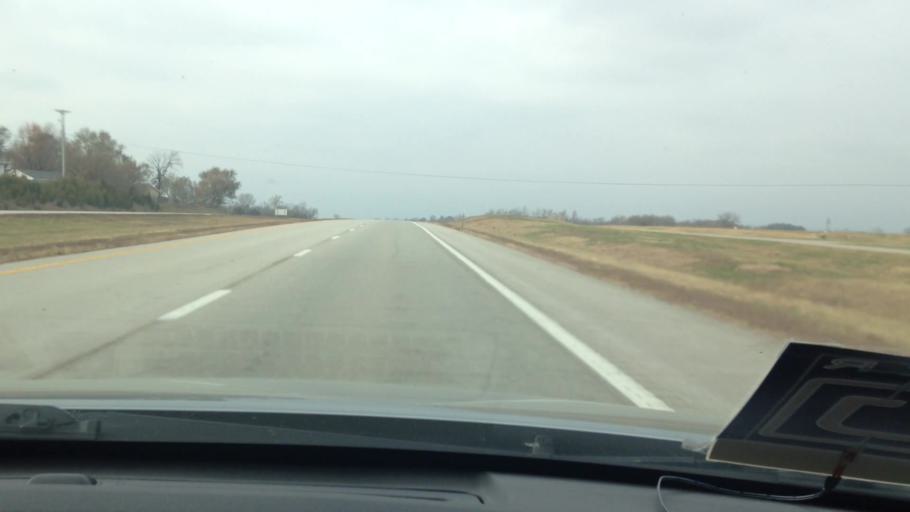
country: US
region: Missouri
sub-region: Cass County
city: Garden City
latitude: 38.5613
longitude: -94.1828
